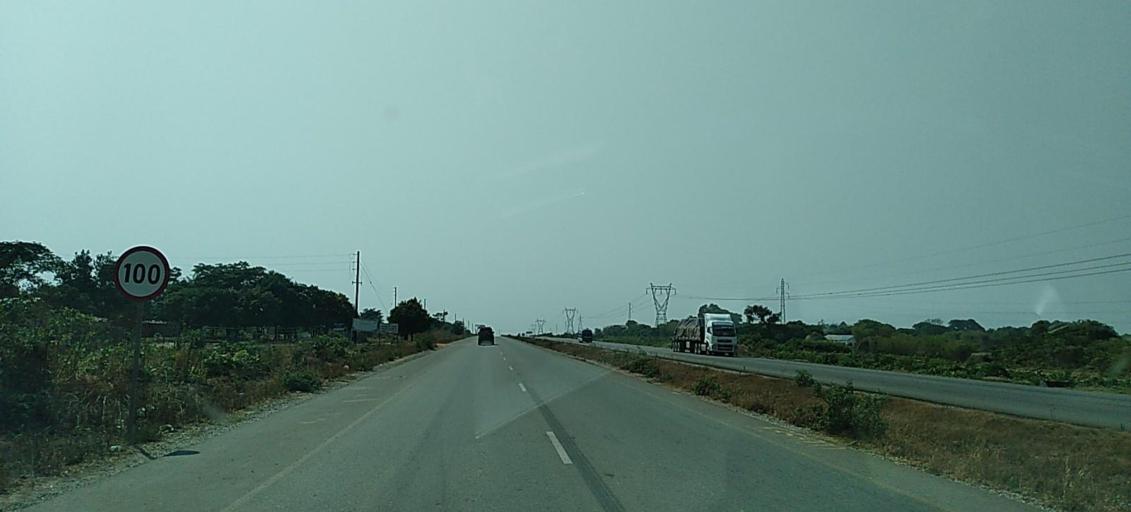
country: ZM
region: Copperbelt
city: Chambishi
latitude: -12.5974
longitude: 27.9601
